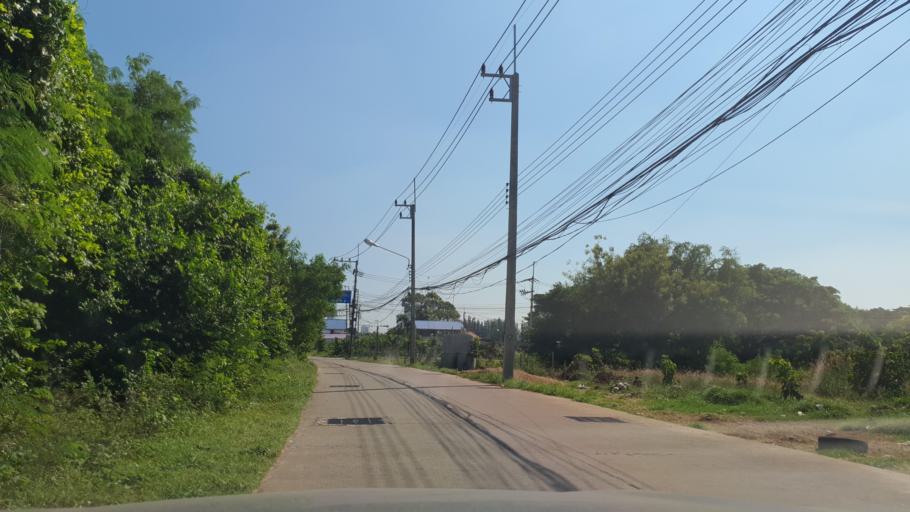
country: TH
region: Chon Buri
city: Phatthaya
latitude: 12.8571
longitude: 100.9010
